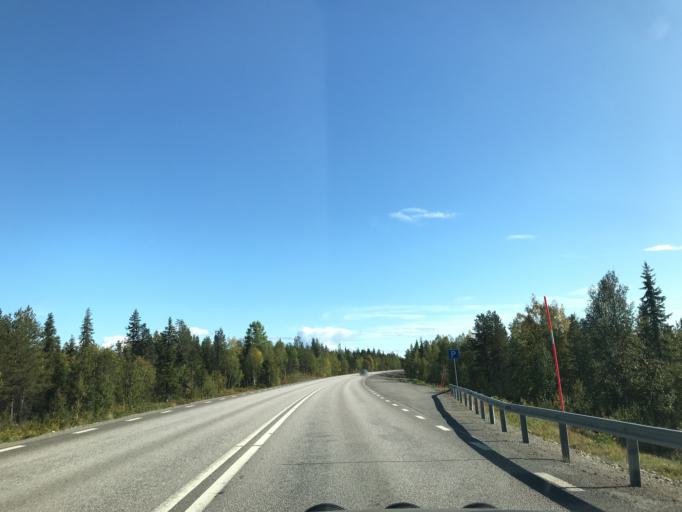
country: SE
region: Norrbotten
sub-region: Gallivare Kommun
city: Malmberget
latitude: 67.6447
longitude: 21.1147
